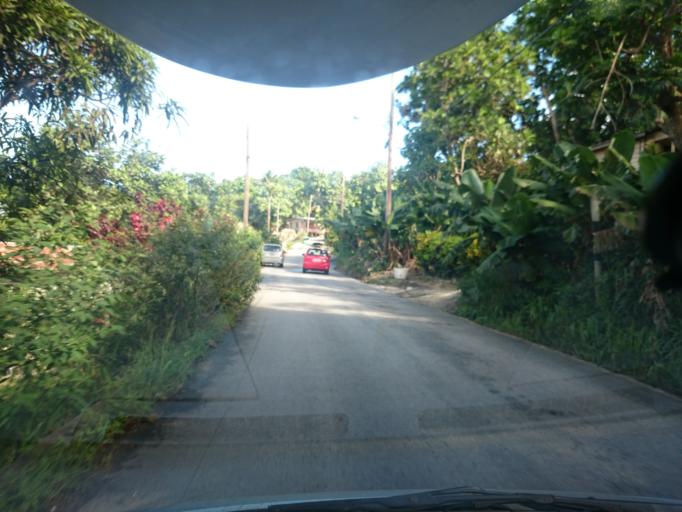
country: BB
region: Saint Joseph
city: Bathsheba
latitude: 13.2075
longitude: -59.5321
